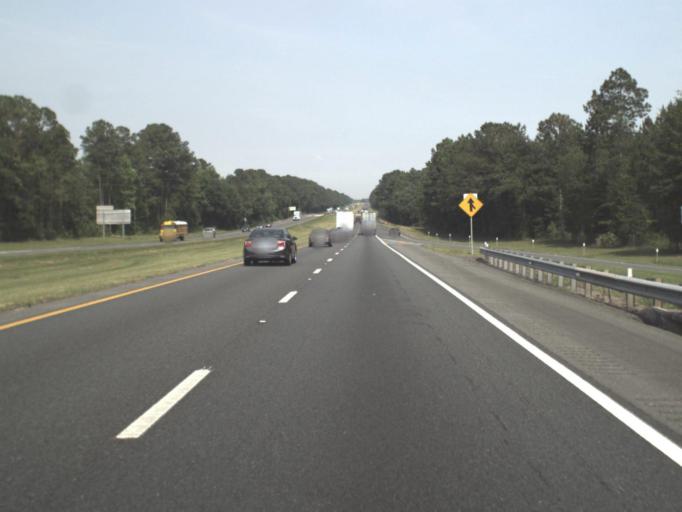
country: US
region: Florida
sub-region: Baker County
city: Macclenny
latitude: 30.2614
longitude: -82.1608
